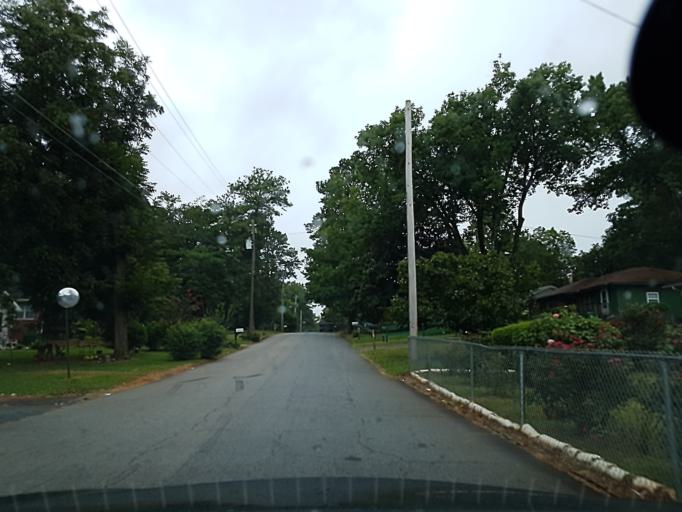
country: US
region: Georgia
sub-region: DeKalb County
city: Candler-McAfee
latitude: 33.7373
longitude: -84.2542
